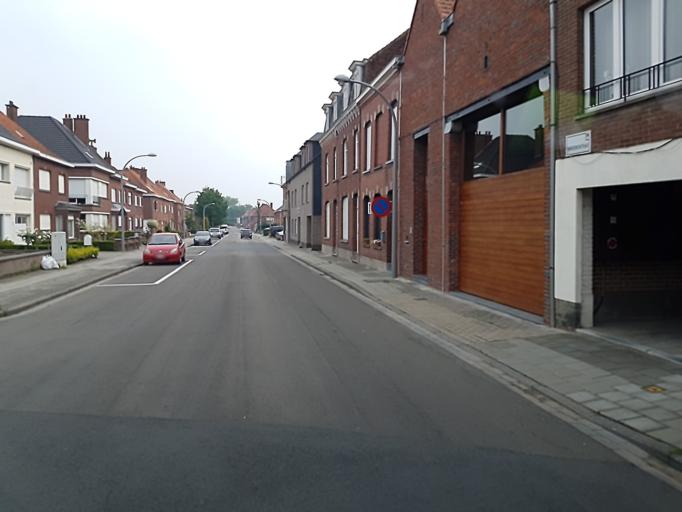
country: BE
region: Flanders
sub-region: Provincie West-Vlaanderen
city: Kortrijk
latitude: 50.8207
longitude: 3.2294
